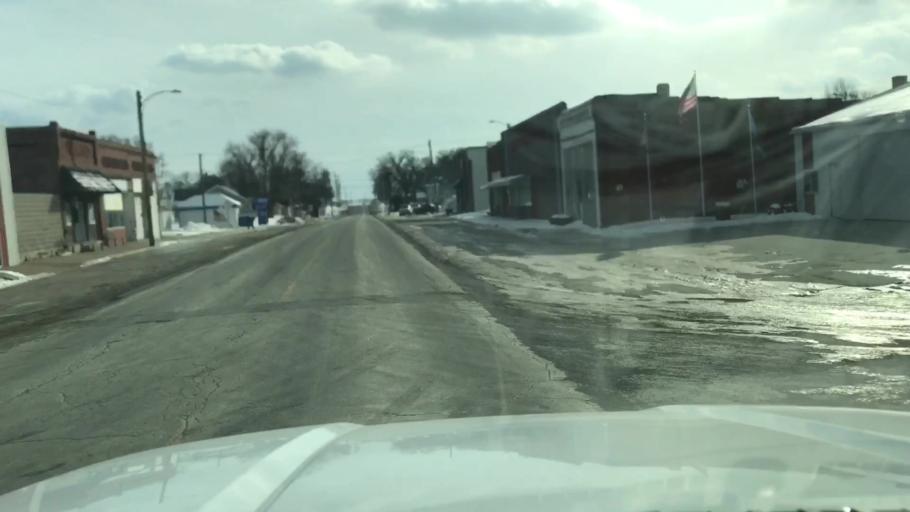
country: US
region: Missouri
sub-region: Gentry County
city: Stanberry
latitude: 40.3521
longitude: -94.6732
